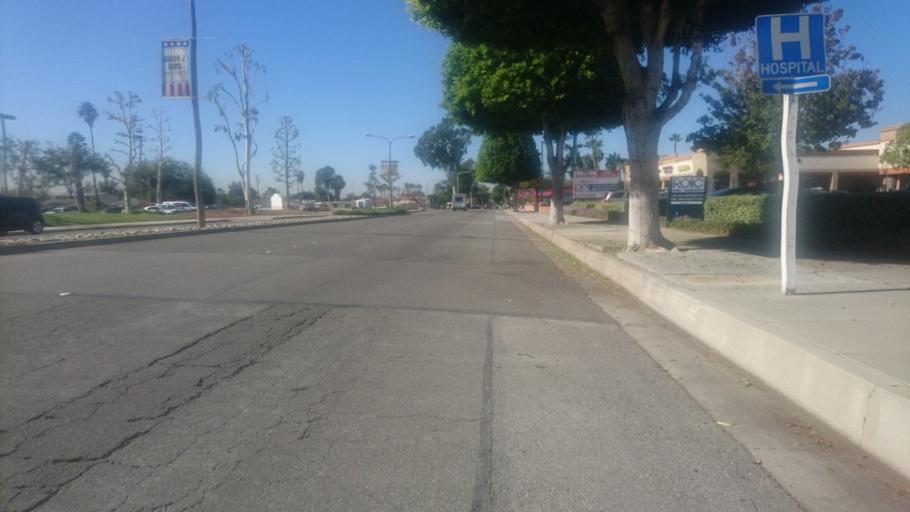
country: US
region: California
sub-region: Los Angeles County
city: Glendora
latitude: 34.1288
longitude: -117.8651
